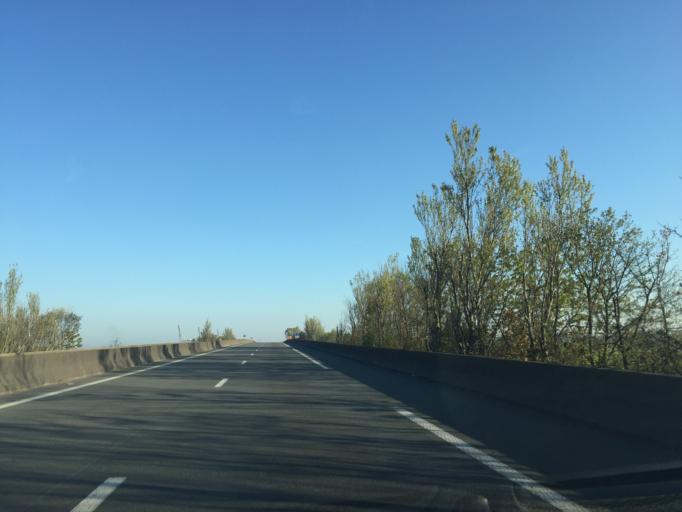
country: FR
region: Nord-Pas-de-Calais
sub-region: Departement du Nord
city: Loon-Plage
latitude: 50.9854
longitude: 2.2084
